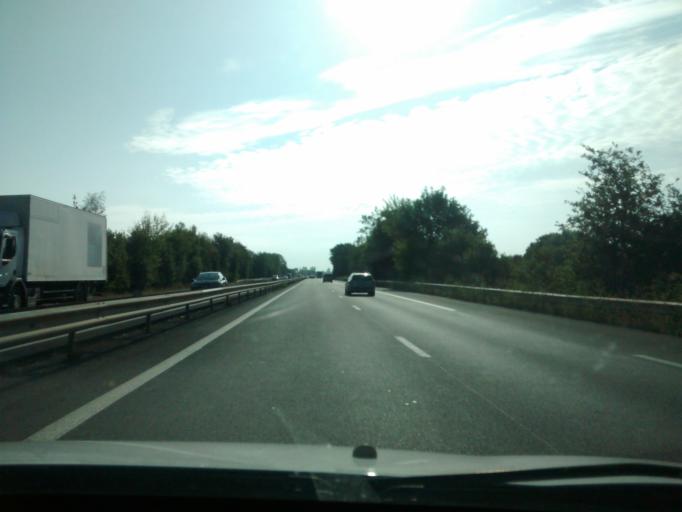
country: FR
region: Brittany
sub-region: Departement d'Ille-et-Vilaine
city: Torce
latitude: 48.0754
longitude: -1.2715
